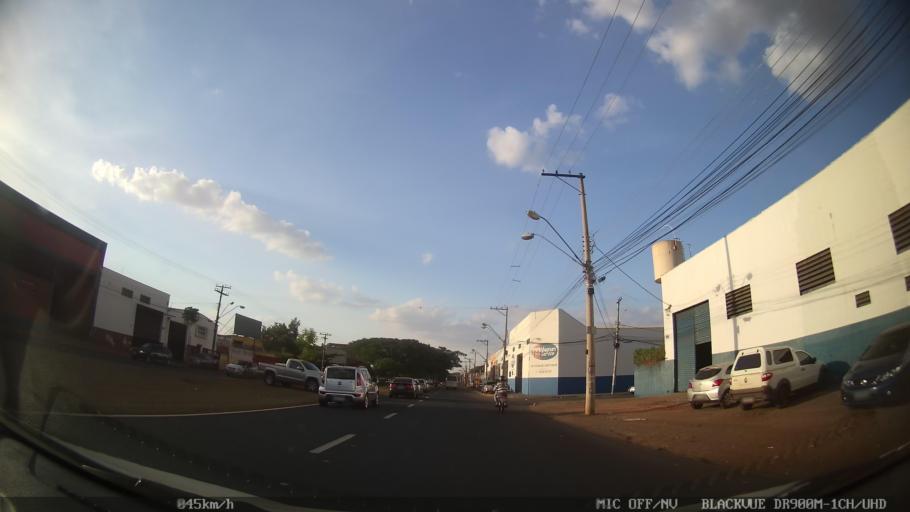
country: BR
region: Sao Paulo
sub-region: Ribeirao Preto
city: Ribeirao Preto
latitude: -21.1352
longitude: -47.7962
